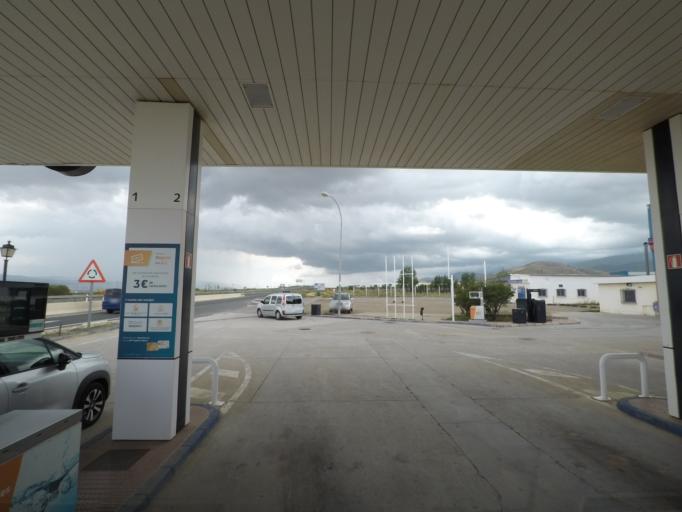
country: ES
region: Andalusia
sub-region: Provincia de Granada
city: Ferreira
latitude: 37.2067
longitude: -3.0483
